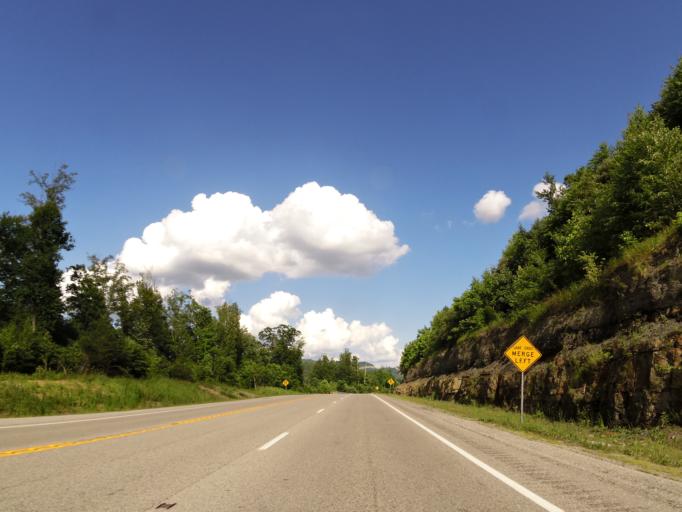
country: US
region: Kentucky
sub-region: Harlan County
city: Harlan
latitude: 36.7903
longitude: -83.2549
